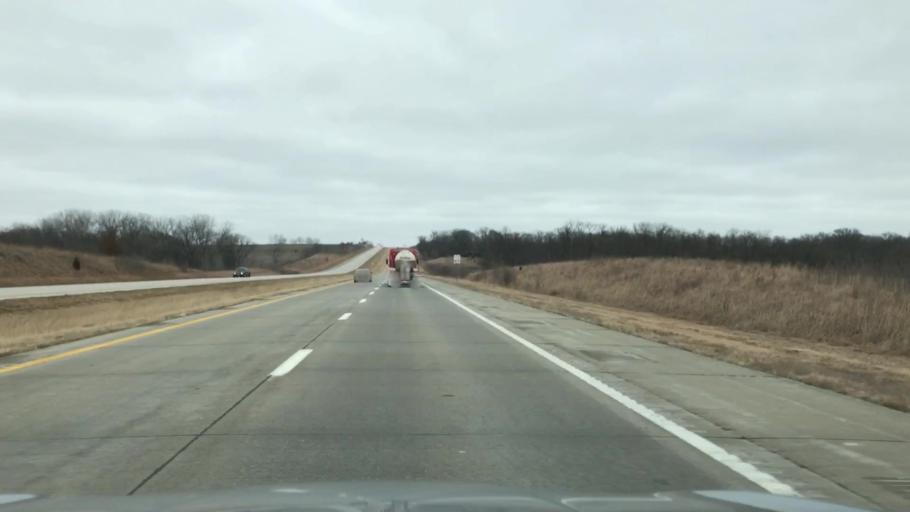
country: US
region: Missouri
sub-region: Caldwell County
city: Hamilton
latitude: 39.7349
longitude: -93.9441
